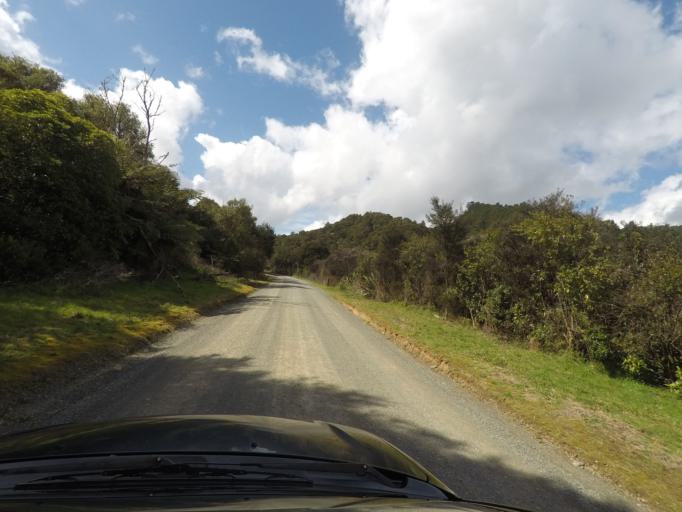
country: NZ
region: Auckland
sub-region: Auckland
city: Red Hill
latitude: -37.0937
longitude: 175.1524
